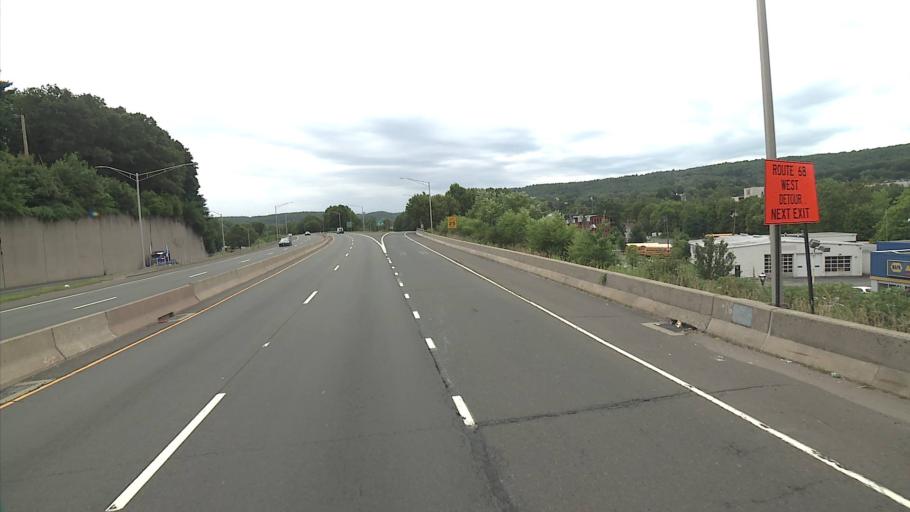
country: US
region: Connecticut
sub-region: New Haven County
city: Naugatuck
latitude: 41.4883
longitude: -73.0519
